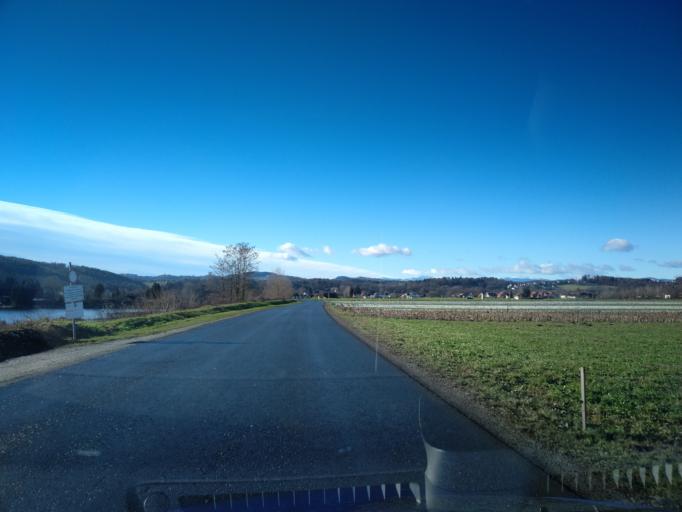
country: AT
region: Styria
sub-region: Politischer Bezirk Leibnitz
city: Kaindorf an der Sulm
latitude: 46.8141
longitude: 15.5317
